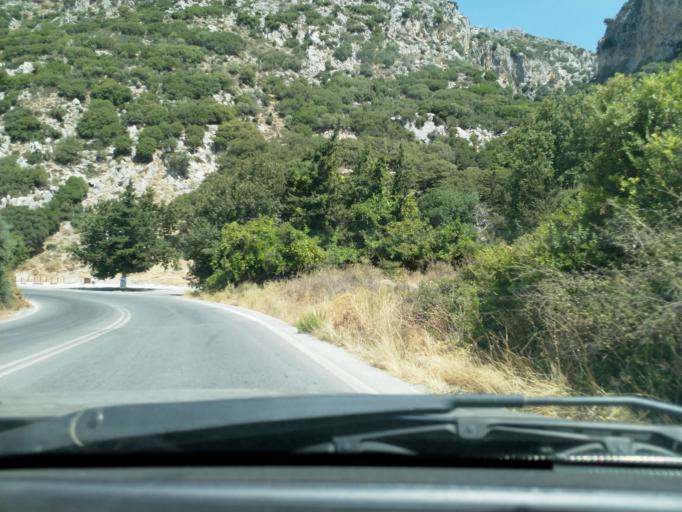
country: GR
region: Crete
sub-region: Nomos Rethymnis
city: Agia Foteini
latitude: 35.2038
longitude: 24.5433
